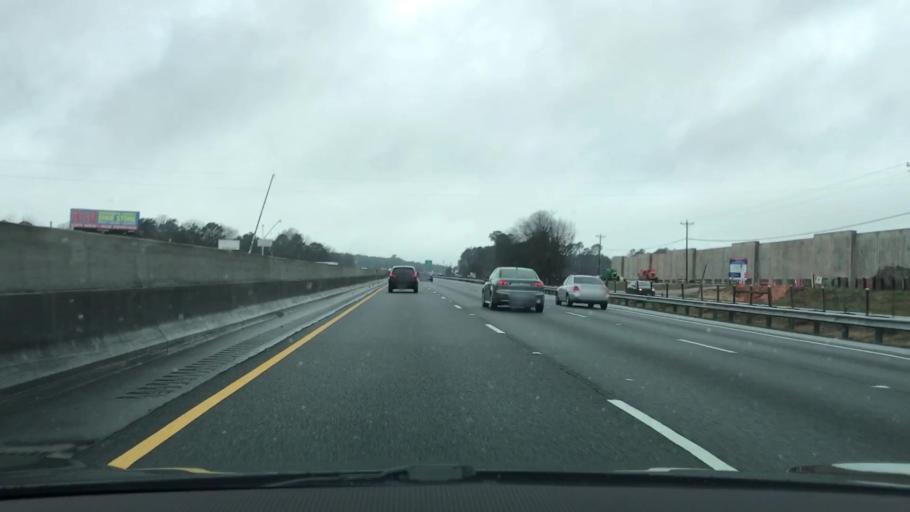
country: US
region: Georgia
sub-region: Rockdale County
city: Conyers
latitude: 33.6306
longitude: -83.9611
